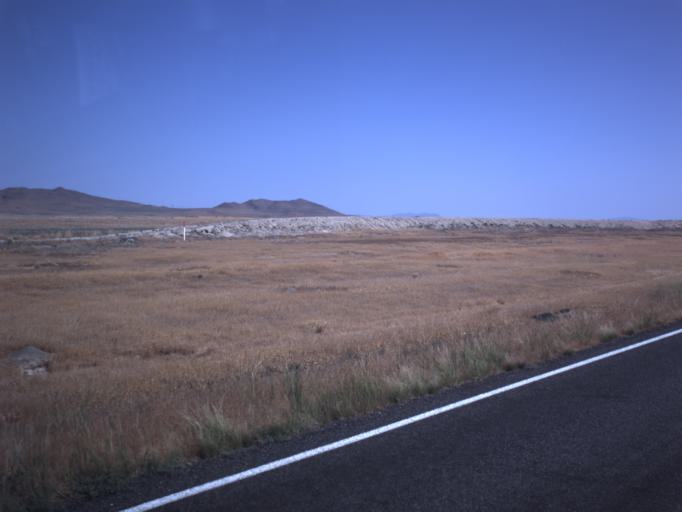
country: US
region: Utah
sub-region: Millard County
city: Delta
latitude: 38.9857
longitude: -112.7932
